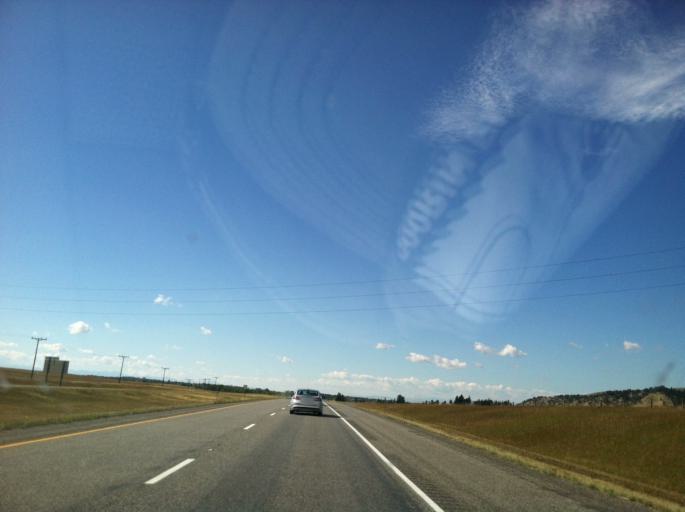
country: US
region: Montana
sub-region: Gallatin County
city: Bozeman
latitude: 45.6630
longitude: -110.9638
